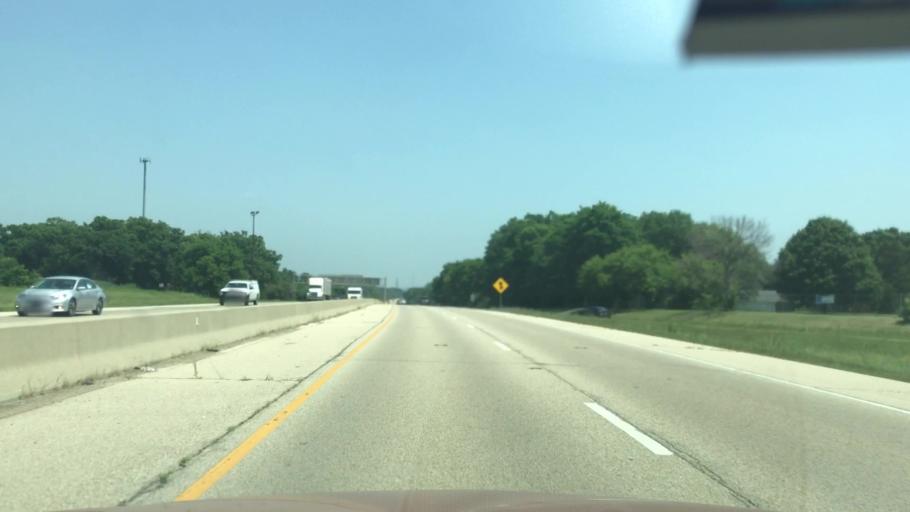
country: US
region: Illinois
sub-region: Winnebago County
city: Cherry Valley
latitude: 42.2390
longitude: -88.9632
